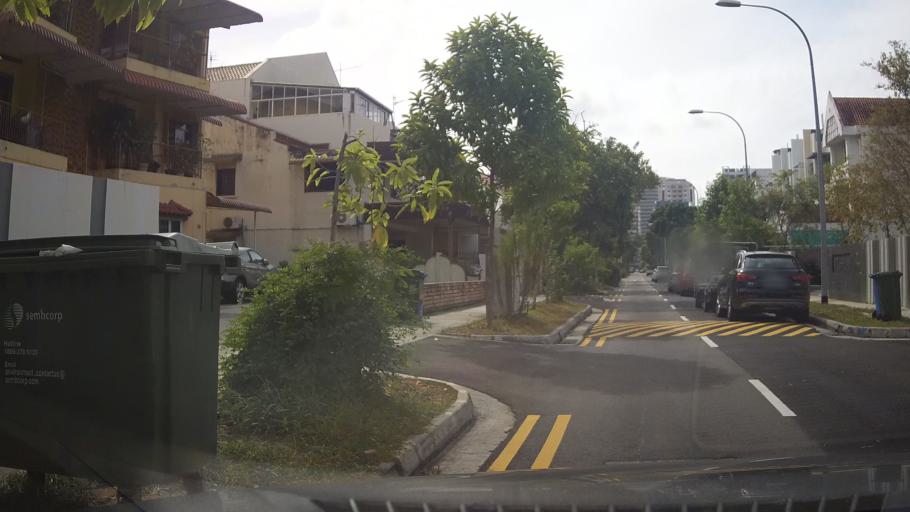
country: SG
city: Singapore
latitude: 1.3084
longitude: 103.9008
